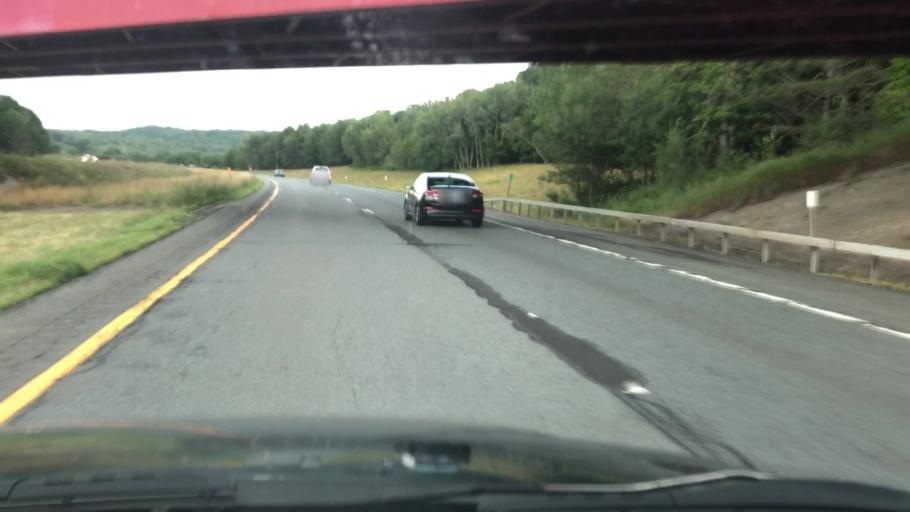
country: US
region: New York
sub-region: Orange County
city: Otisville
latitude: 41.3820
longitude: -74.5815
